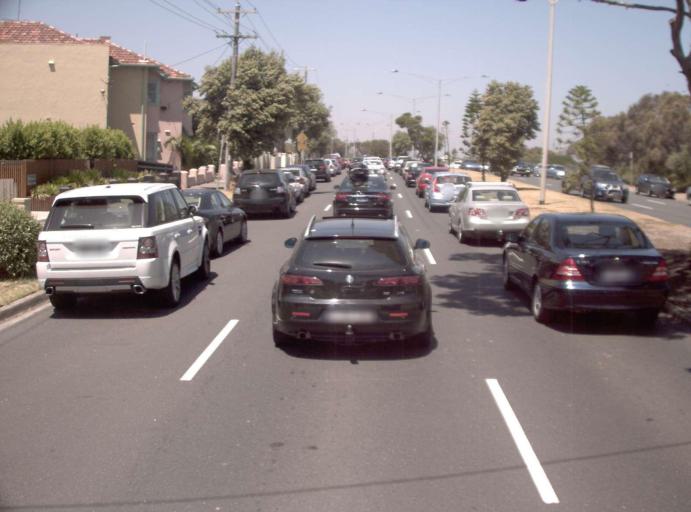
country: AU
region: Victoria
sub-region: Port Phillip
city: Elwood
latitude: -37.8830
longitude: 144.9787
